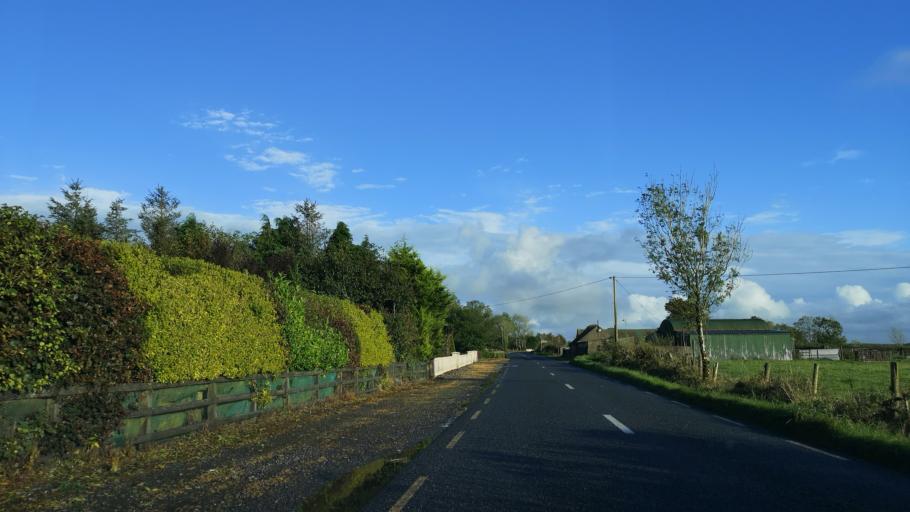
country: IE
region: Connaught
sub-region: Roscommon
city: Castlerea
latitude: 53.8088
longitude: -8.5173
